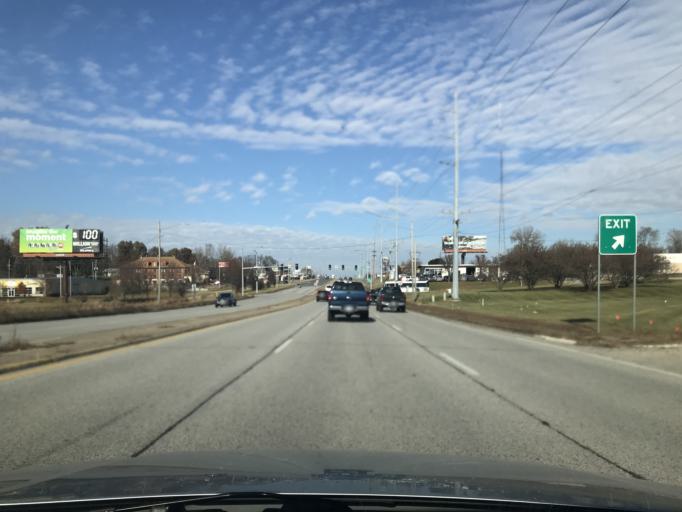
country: US
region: Iowa
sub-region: Scott County
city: Davenport
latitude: 41.5787
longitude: -90.5714
